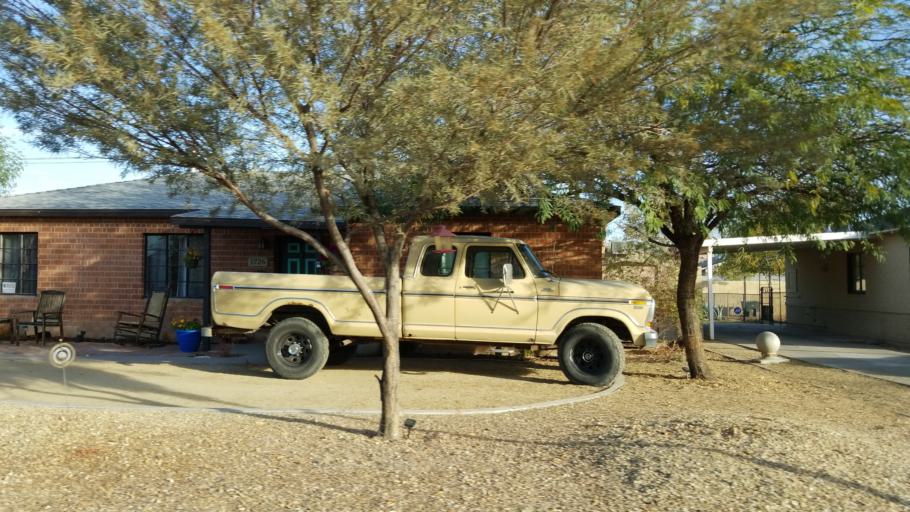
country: US
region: Arizona
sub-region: Maricopa County
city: Phoenix
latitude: 33.4879
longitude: -112.0970
